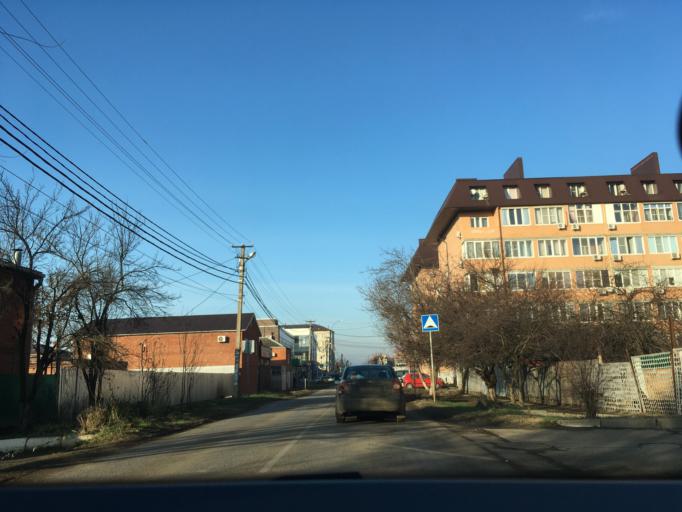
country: RU
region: Krasnodarskiy
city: Krasnodar
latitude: 45.0740
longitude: 39.0212
